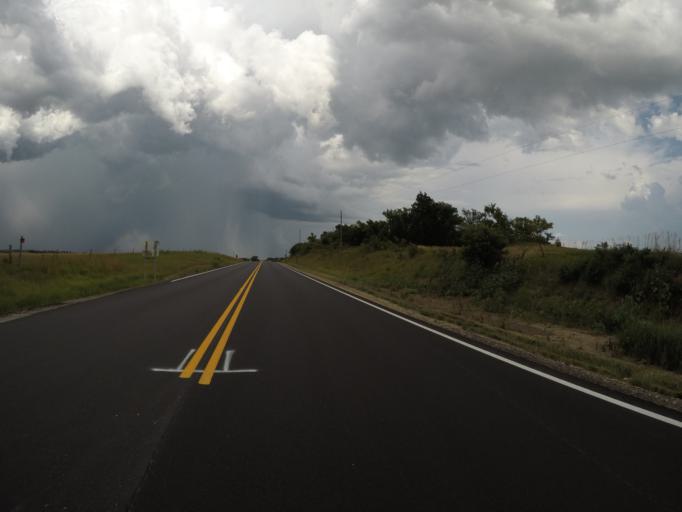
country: US
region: Kansas
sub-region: Clay County
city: Clay Center
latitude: 39.4369
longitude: -96.8364
